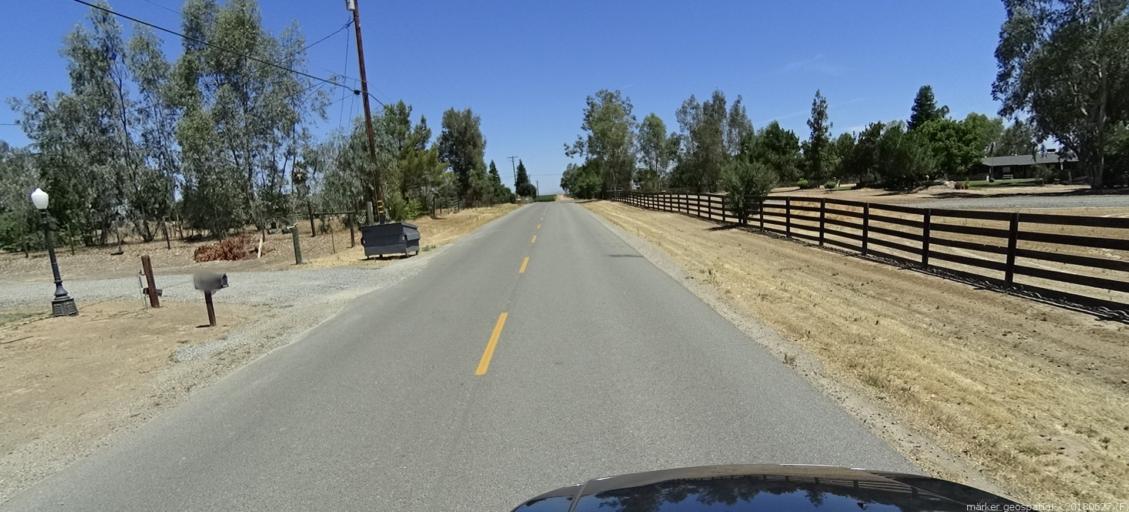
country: US
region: California
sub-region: Madera County
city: Bonadelle Ranchos-Madera Ranchos
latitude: 36.9346
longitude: -119.8625
